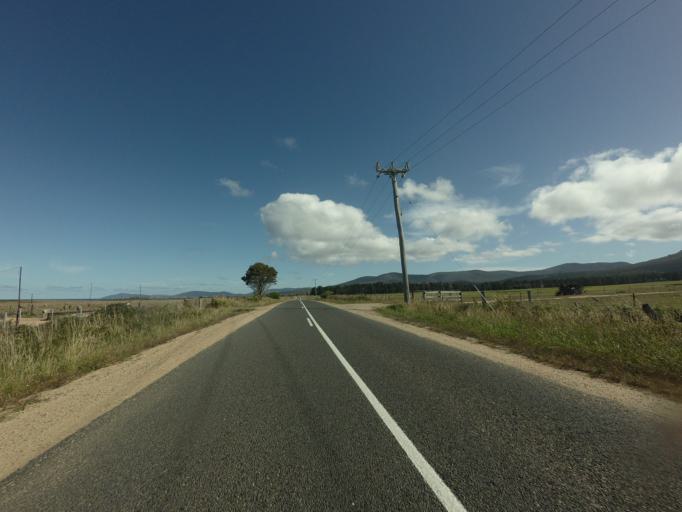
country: AU
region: Tasmania
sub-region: Break O'Day
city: St Helens
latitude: -41.7507
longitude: 148.2774
